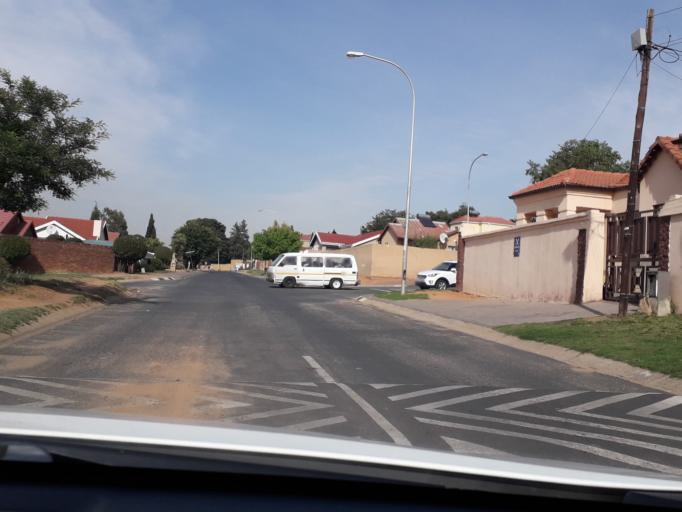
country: ZA
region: Gauteng
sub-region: City of Johannesburg Metropolitan Municipality
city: Modderfontein
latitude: -26.1198
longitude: 28.1017
